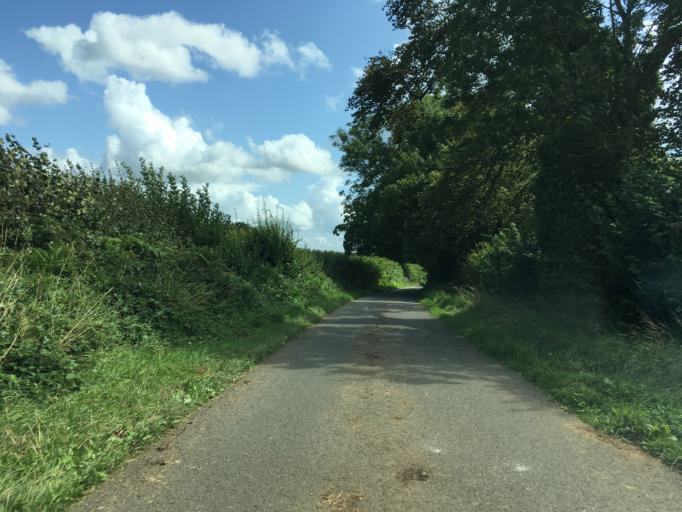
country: GB
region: England
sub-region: Wiltshire
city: Luckington
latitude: 51.6034
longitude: -2.2481
